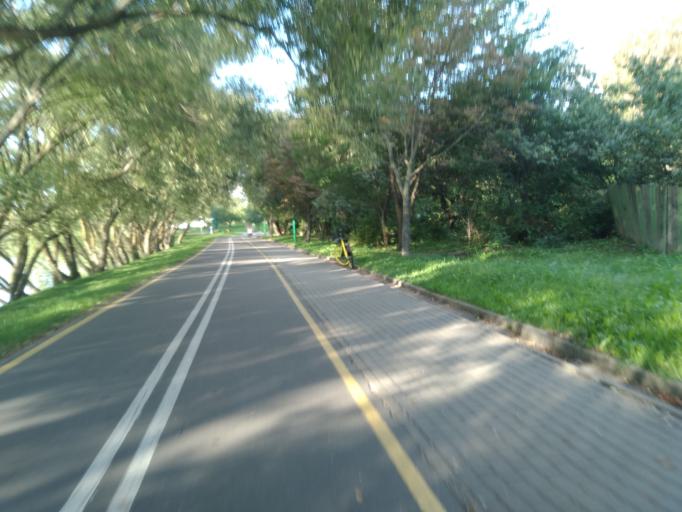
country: BY
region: Minsk
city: Minsk
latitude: 53.8795
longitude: 27.5750
